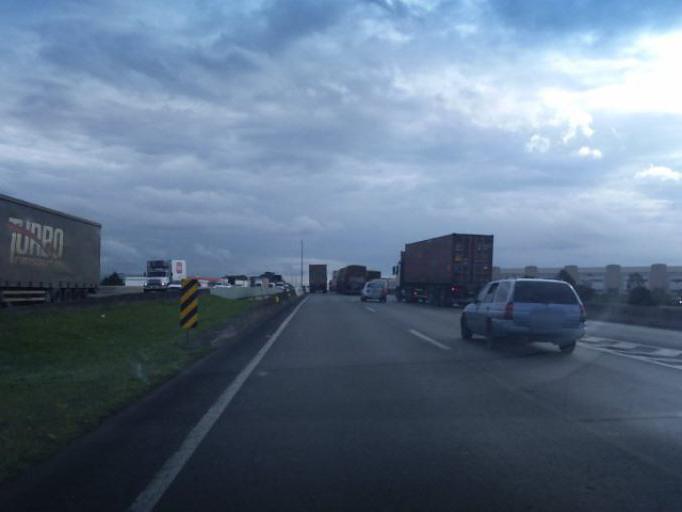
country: BR
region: Parana
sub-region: Sao Jose Dos Pinhais
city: Sao Jose dos Pinhais
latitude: -25.5109
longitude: -49.1276
